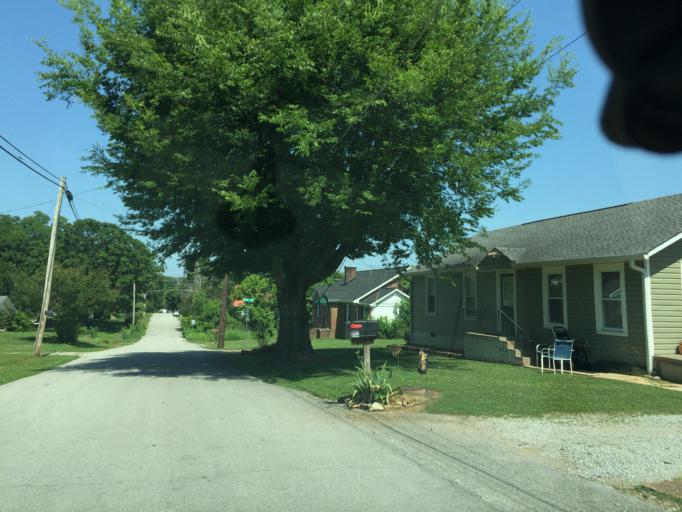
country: US
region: Tennessee
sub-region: Hamilton County
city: Collegedale
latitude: 35.0721
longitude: -85.0586
